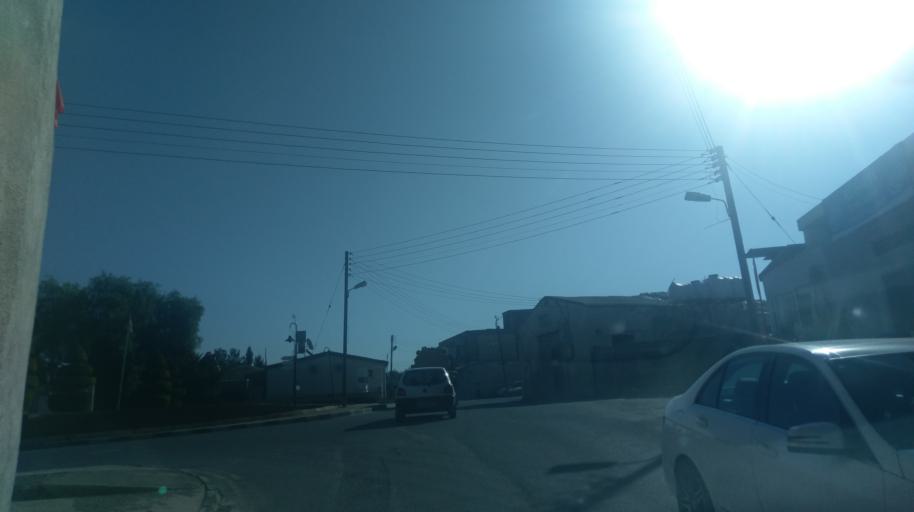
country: CY
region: Keryneia
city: Kyrenia
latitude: 35.2666
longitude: 33.3225
